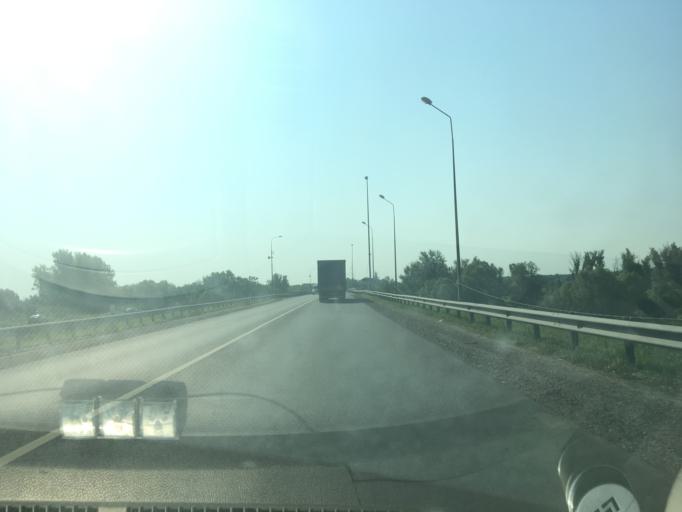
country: RU
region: Nizjnij Novgorod
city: Kstovo
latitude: 56.0989
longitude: 44.3082
